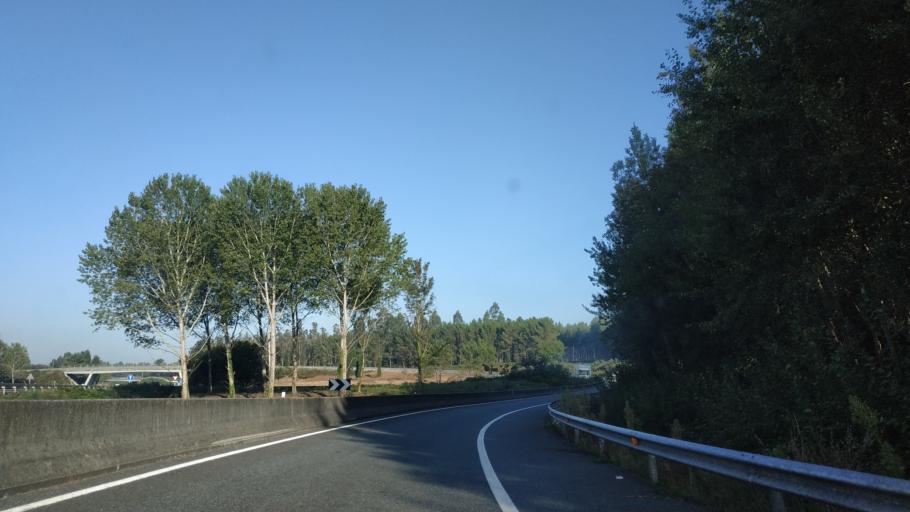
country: ES
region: Galicia
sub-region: Provincia da Coruna
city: Carballo
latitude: 43.2452
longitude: -8.6706
